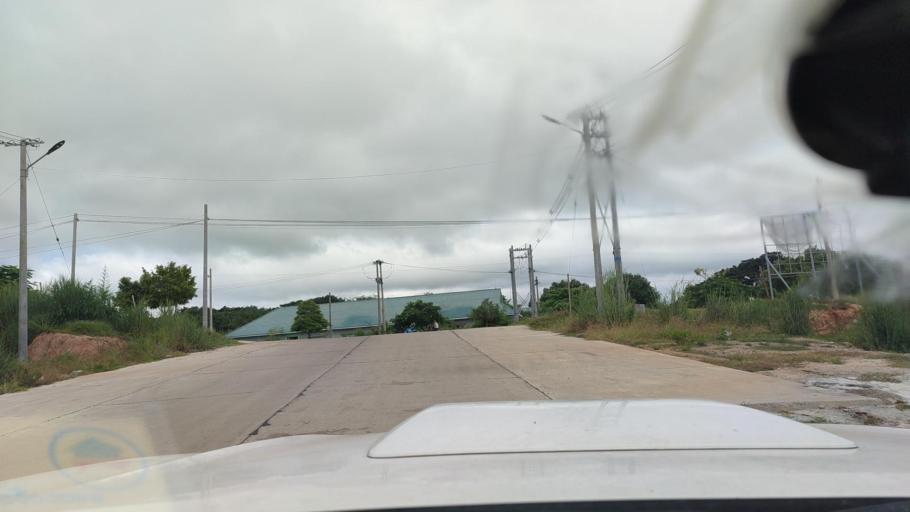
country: MM
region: Mandalay
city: Nay Pyi Taw
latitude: 19.7470
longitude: 96.0686
